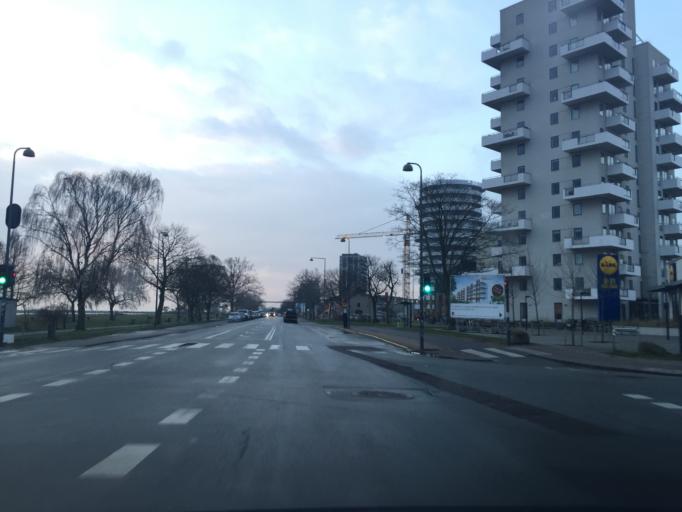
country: DK
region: Capital Region
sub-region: Kobenhavn
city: Christianshavn
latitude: 55.6623
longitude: 12.6316
